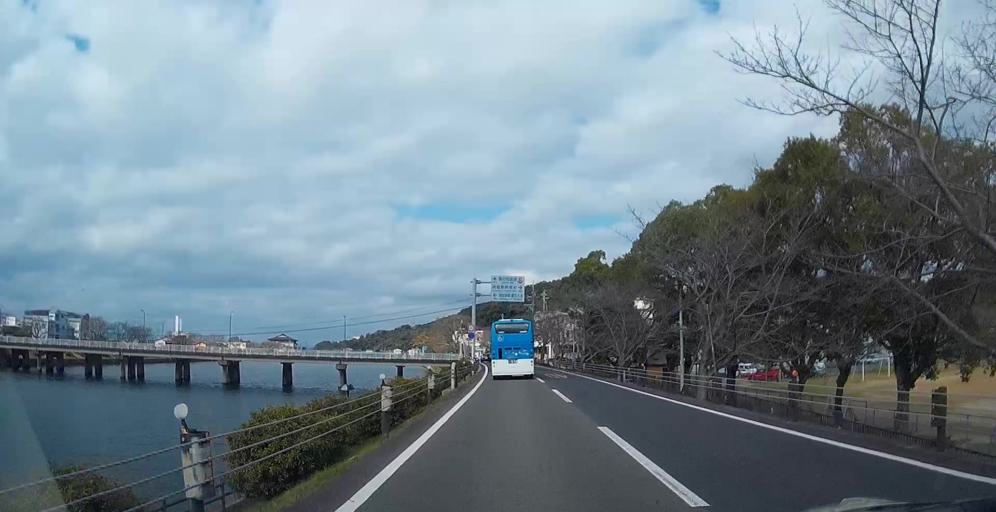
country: JP
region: Kumamoto
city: Minamata
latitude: 32.2135
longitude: 130.4068
